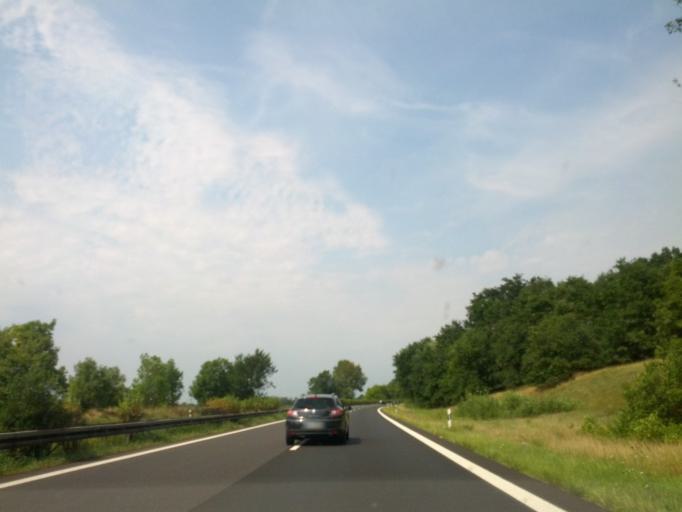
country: DE
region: Brandenburg
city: Wustermark
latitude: 52.5087
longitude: 12.9602
